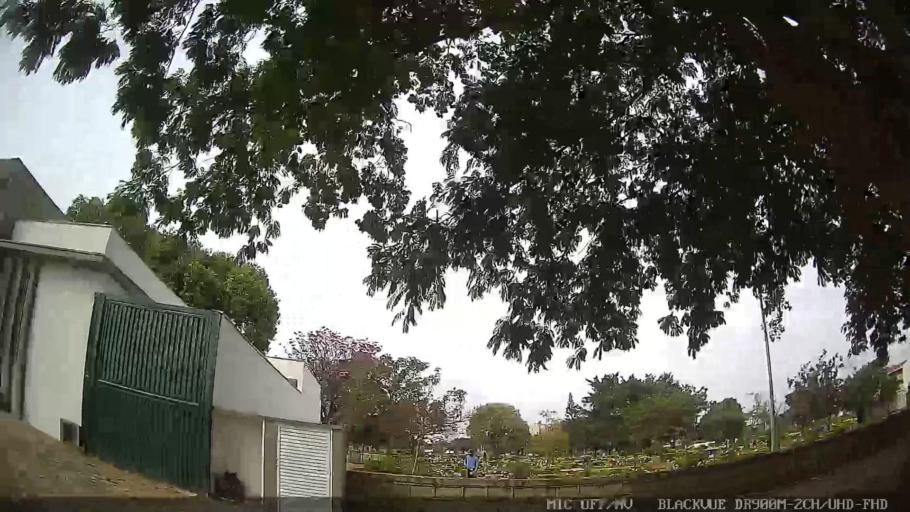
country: BR
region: Sao Paulo
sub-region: Indaiatuba
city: Indaiatuba
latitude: -23.0955
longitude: -47.2103
